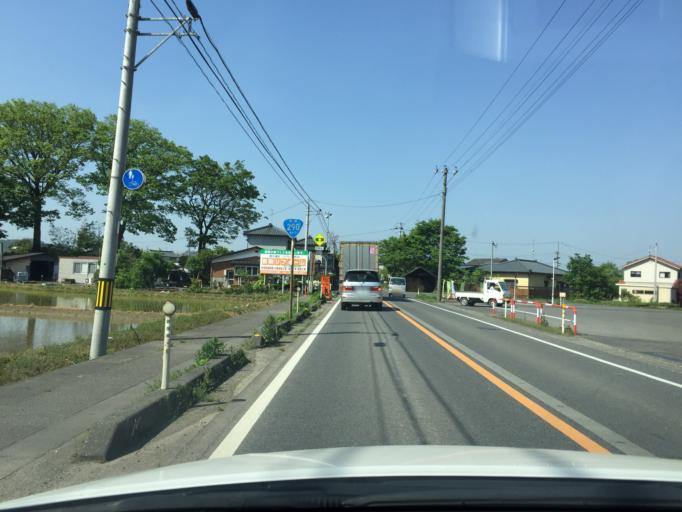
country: JP
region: Niigata
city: Muramatsu
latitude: 37.7061
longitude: 139.2001
